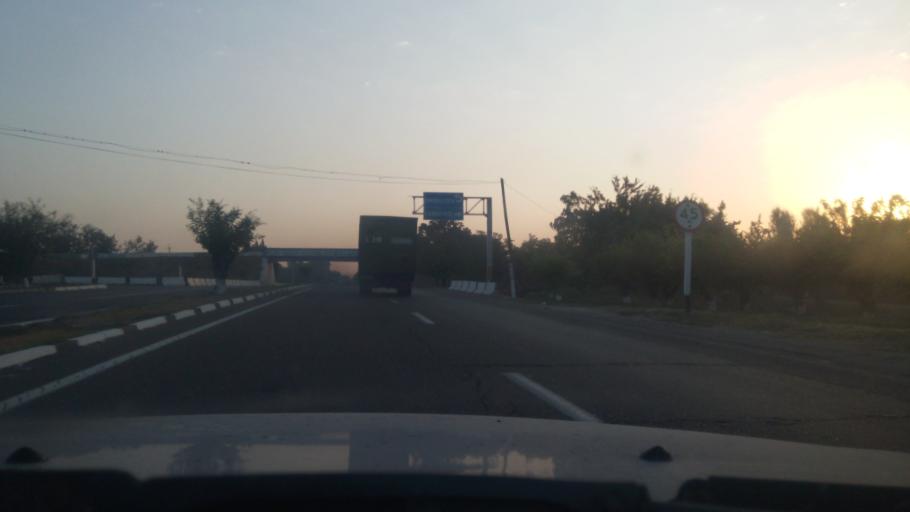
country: UZ
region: Toshkent
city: Yangiyul
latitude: 41.1048
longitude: 68.9727
